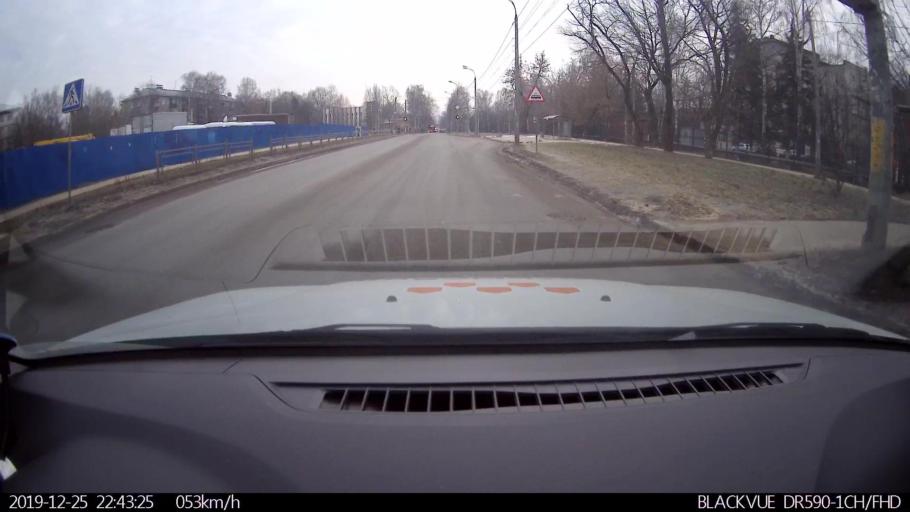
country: RU
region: Nizjnij Novgorod
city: Gorbatovka
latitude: 56.2325
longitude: 43.8458
